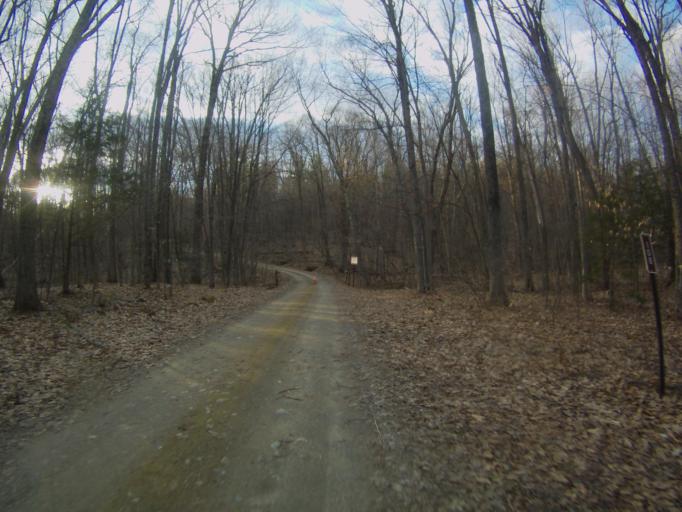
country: US
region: Vermont
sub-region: Rutland County
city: Brandon
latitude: 43.8461
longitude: -73.0295
